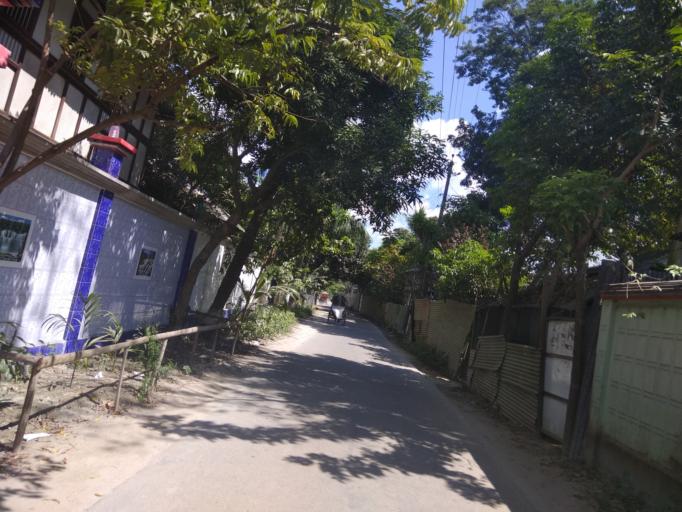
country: BD
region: Dhaka
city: Narayanganj
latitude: 23.4405
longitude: 90.4844
